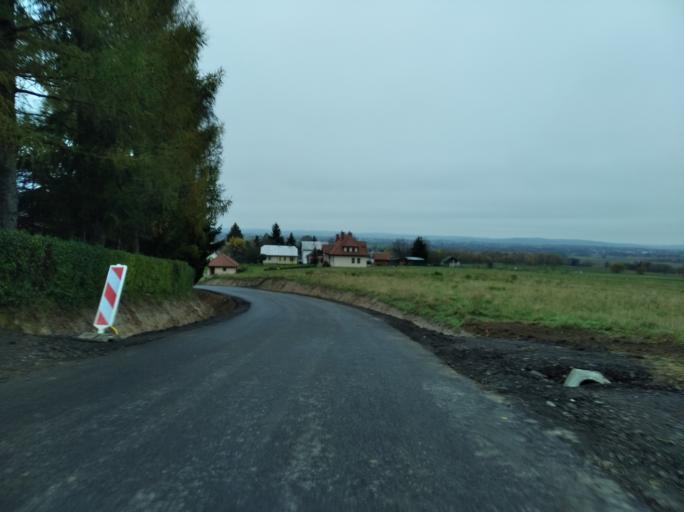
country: PL
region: Subcarpathian Voivodeship
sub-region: Powiat krosnienski
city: Odrzykon
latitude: 49.7366
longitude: 21.7728
